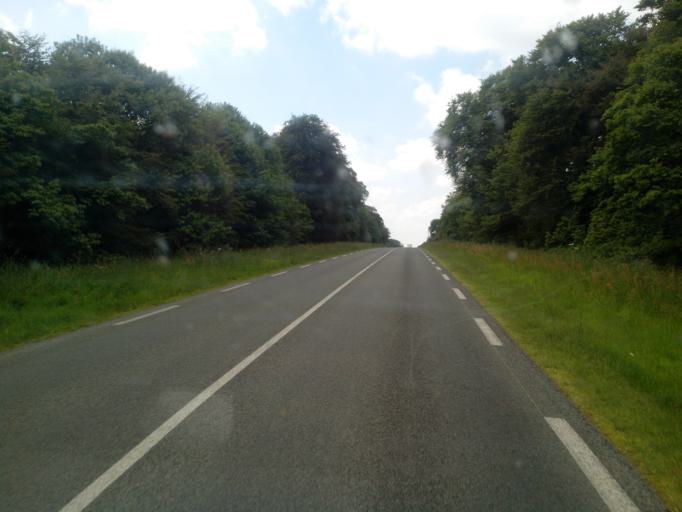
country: FR
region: Brittany
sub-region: Departement d'Ille-et-Vilaine
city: Landean
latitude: 48.3809
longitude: -1.1728
